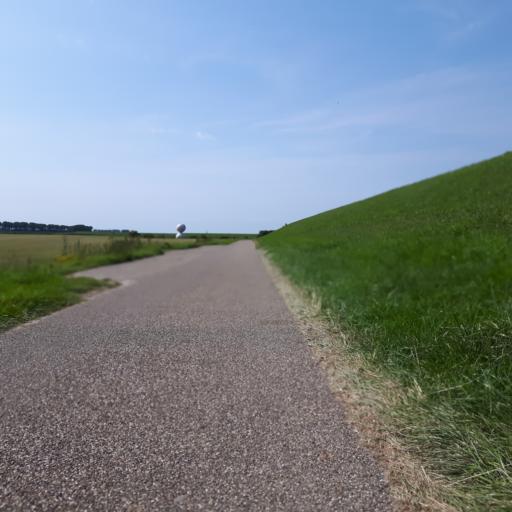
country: NL
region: Zeeland
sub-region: Gemeente Goes
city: Goes
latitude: 51.5435
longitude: 3.9205
